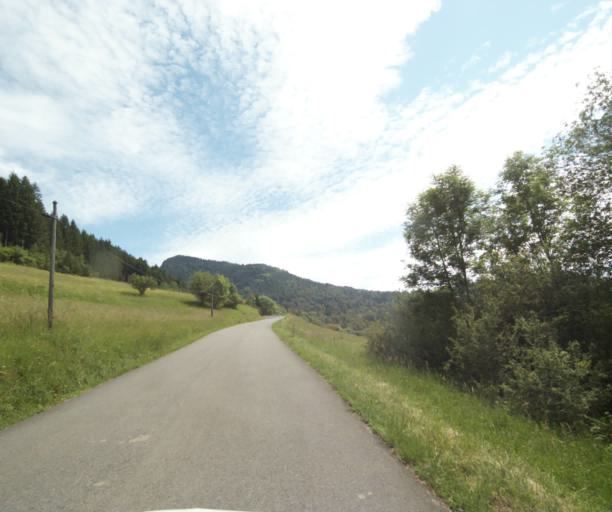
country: FR
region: Rhone-Alpes
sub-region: Departement de la Haute-Savoie
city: Perrignier
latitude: 46.2933
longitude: 6.4752
